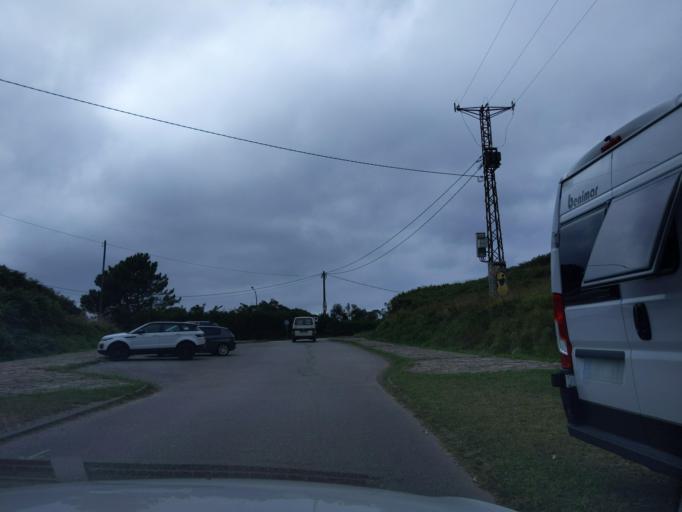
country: ES
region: Asturias
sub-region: Province of Asturias
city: Aviles
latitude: 43.6007
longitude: -5.9158
